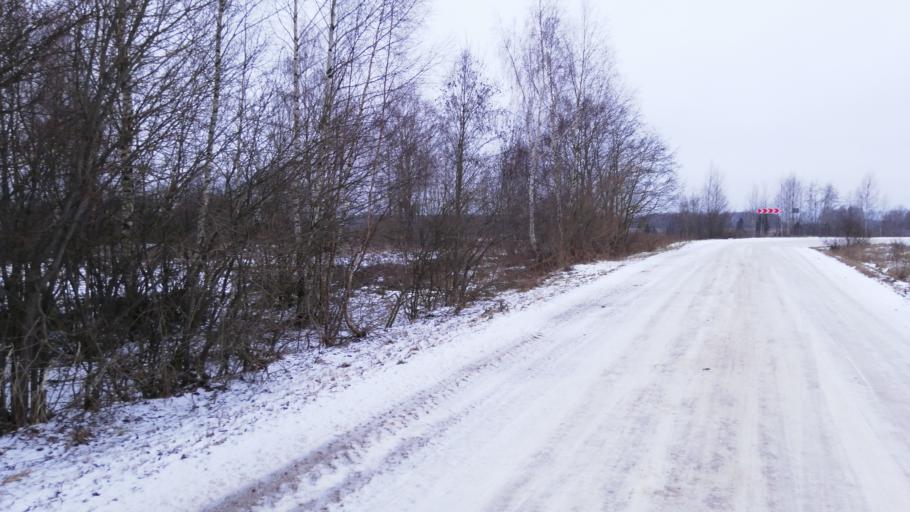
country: RU
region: Kostroma
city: Oktyabr'skiy
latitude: 57.6917
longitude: 41.1711
